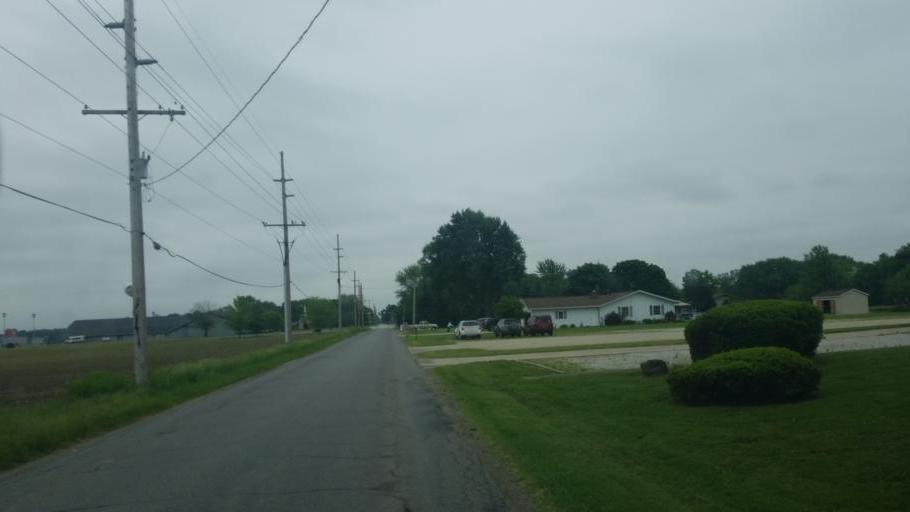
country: US
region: Indiana
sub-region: Elkhart County
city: Nappanee
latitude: 41.4571
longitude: -86.0059
